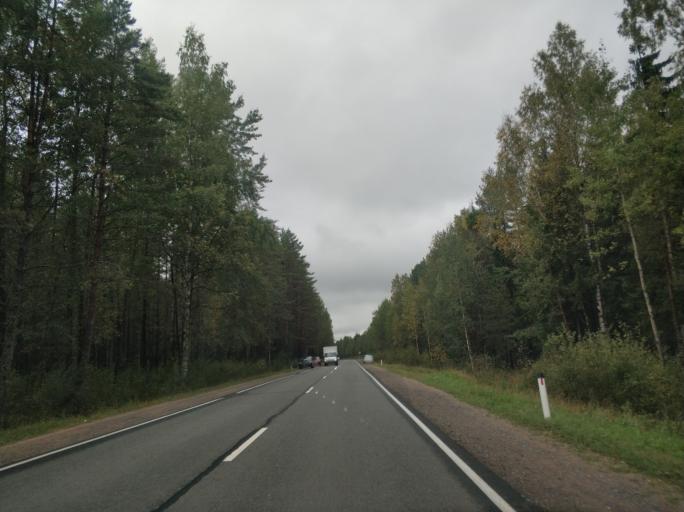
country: RU
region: Leningrad
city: Shcheglovo
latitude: 60.1015
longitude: 30.8274
